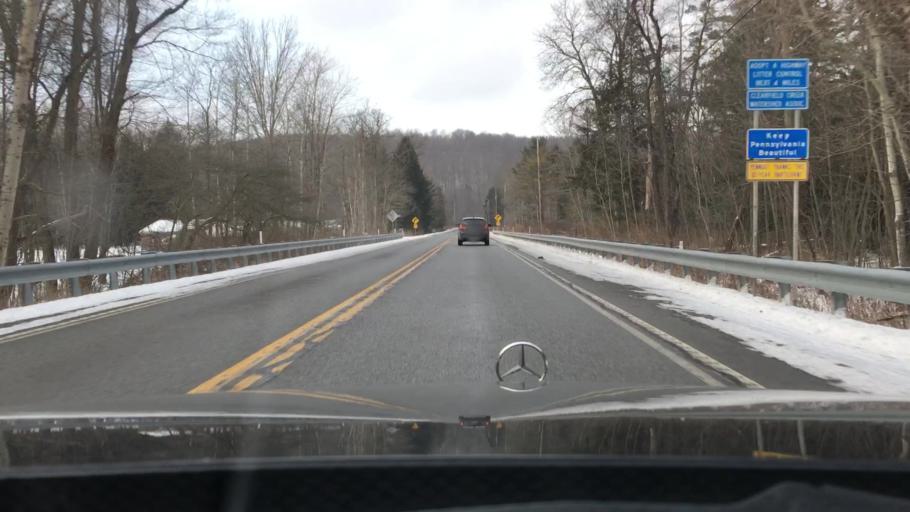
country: US
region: Pennsylvania
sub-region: Cambria County
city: Gallitzin
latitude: 40.5092
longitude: -78.5823
